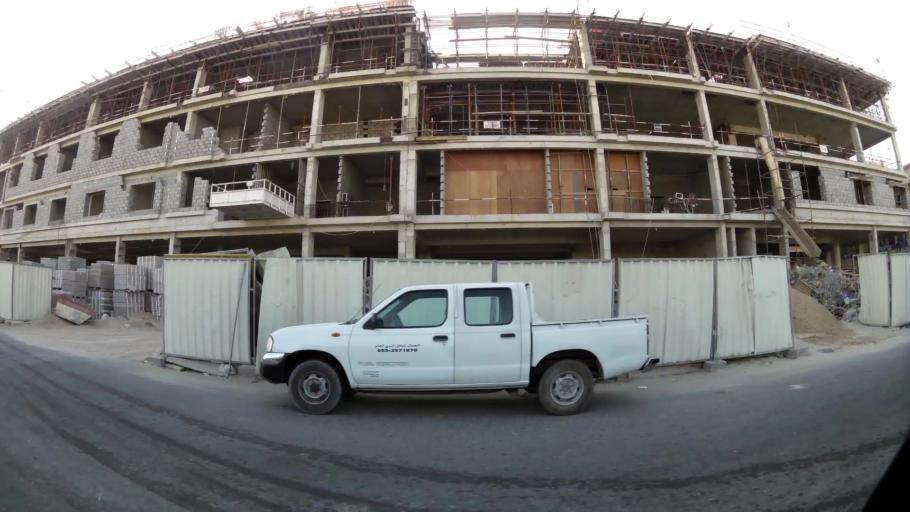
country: AE
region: Dubai
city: Dubai
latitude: 25.1302
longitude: 55.2388
